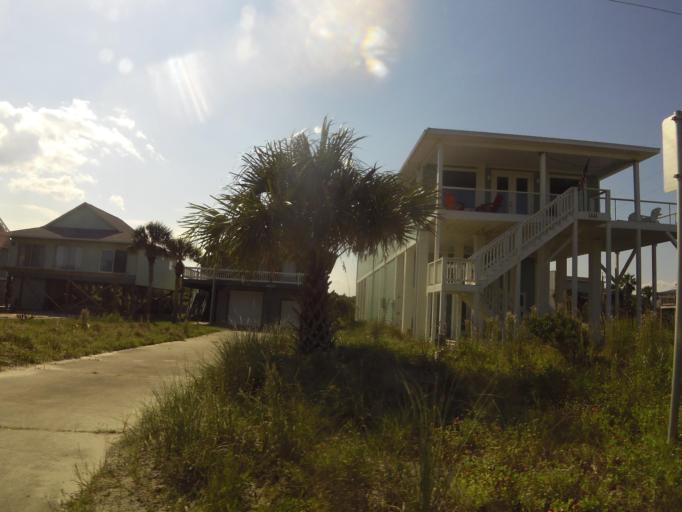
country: US
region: Florida
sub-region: Nassau County
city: Fernandina Beach
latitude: 30.6854
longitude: -81.4293
